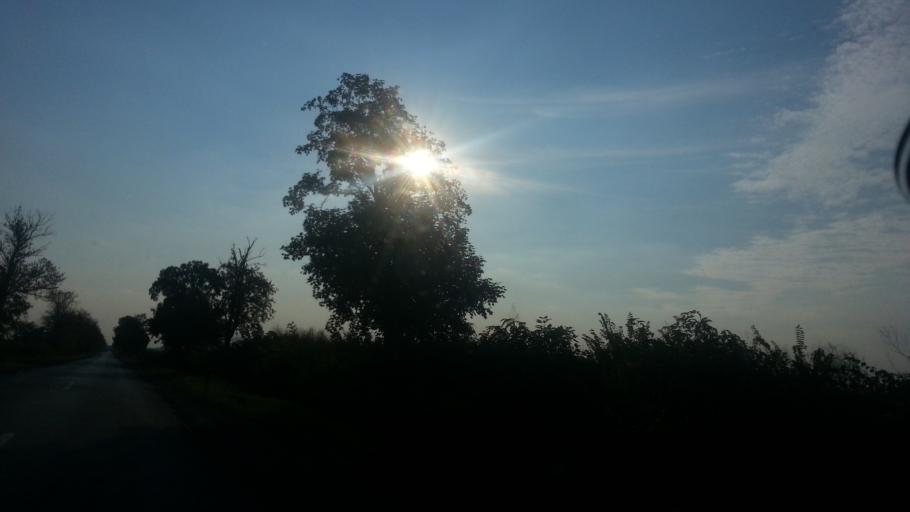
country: RS
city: Novi Karlovci
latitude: 45.0986
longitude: 20.2032
